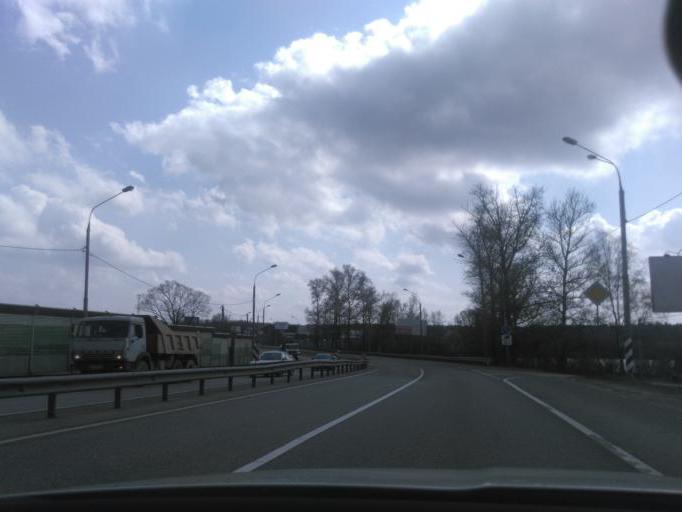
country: RU
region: Moskovskaya
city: Chashnikovo
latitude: 56.0335
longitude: 37.1641
